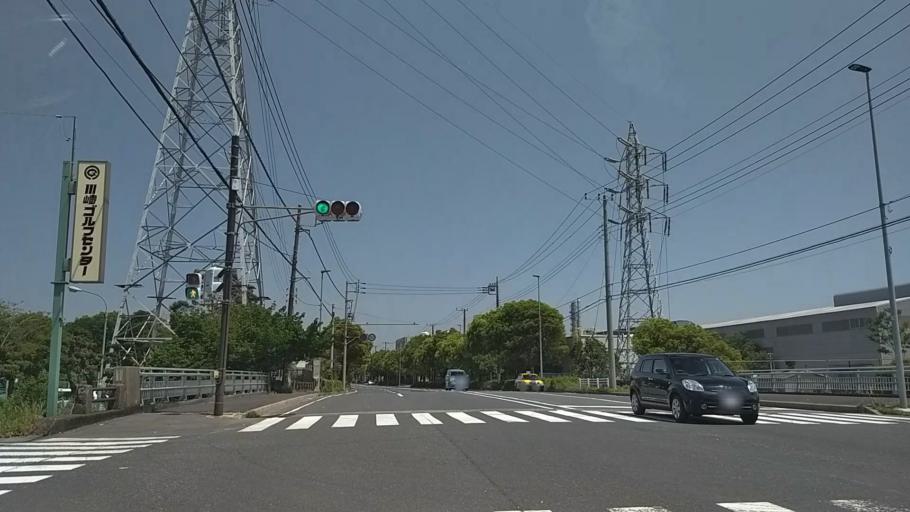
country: JP
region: Kanagawa
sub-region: Kawasaki-shi
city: Kawasaki
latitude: 35.5208
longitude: 139.7433
